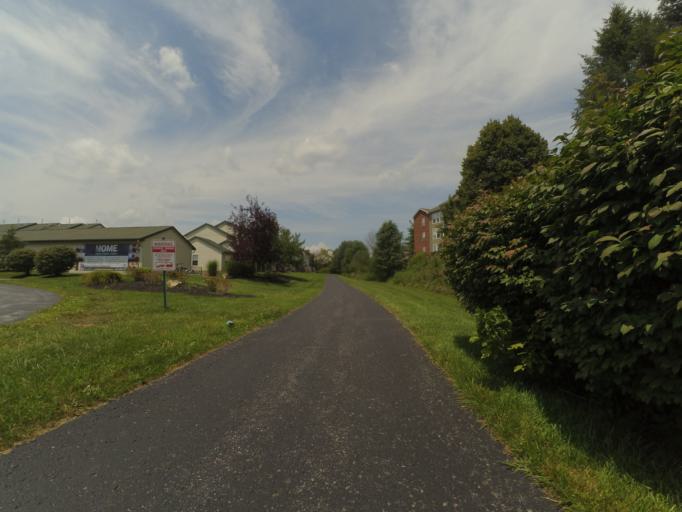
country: US
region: Pennsylvania
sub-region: Centre County
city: State College
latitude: 40.7988
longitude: -77.8881
